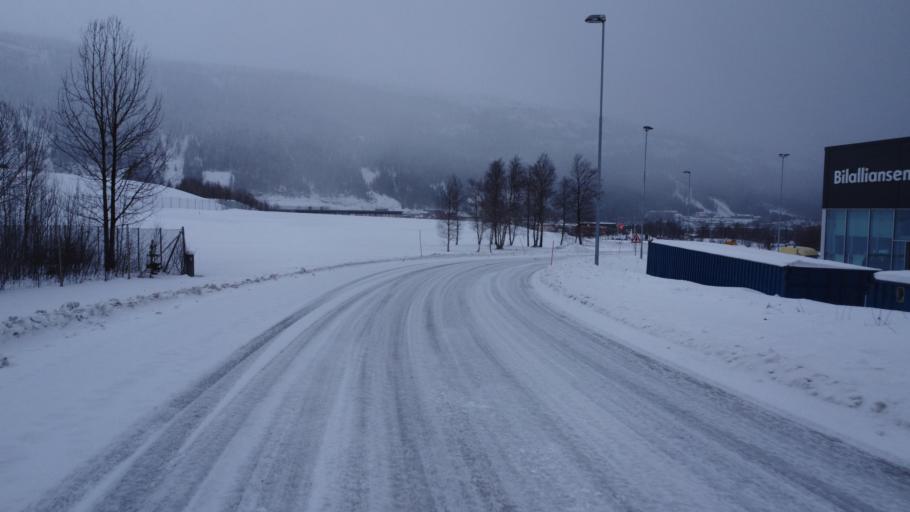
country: NO
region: Nordland
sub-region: Rana
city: Mo i Rana
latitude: 66.3108
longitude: 14.1567
